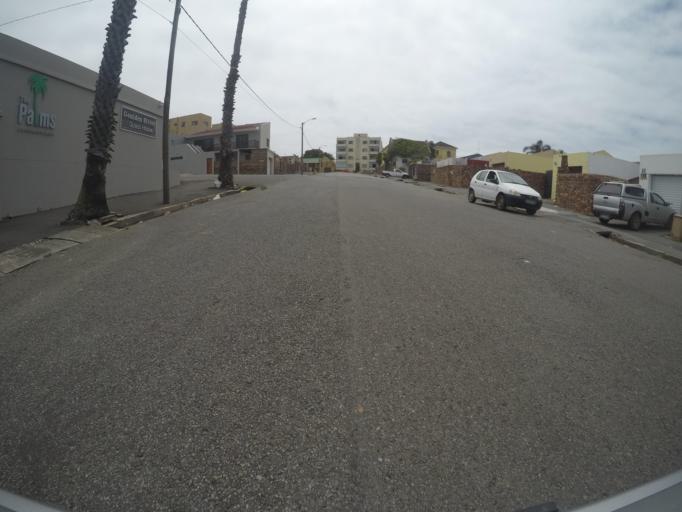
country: ZA
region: Eastern Cape
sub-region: Buffalo City Metropolitan Municipality
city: East London
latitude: -33.0196
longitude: 27.9168
